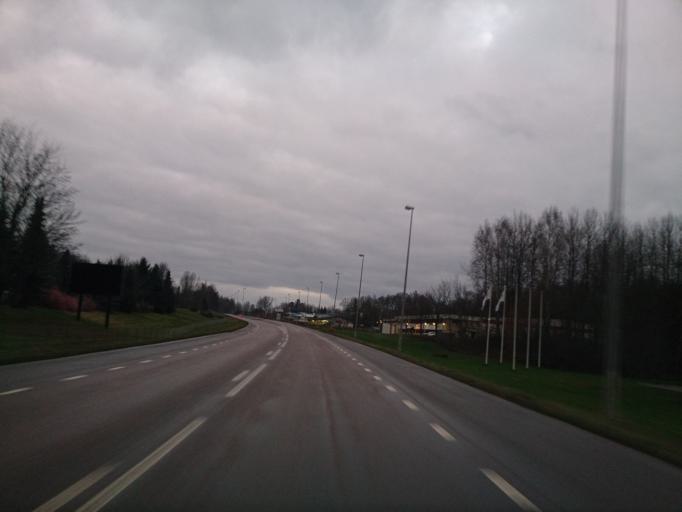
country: SE
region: OEstergoetland
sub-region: Atvidabergs Kommun
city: Atvidaberg
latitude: 58.2116
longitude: 15.9855
